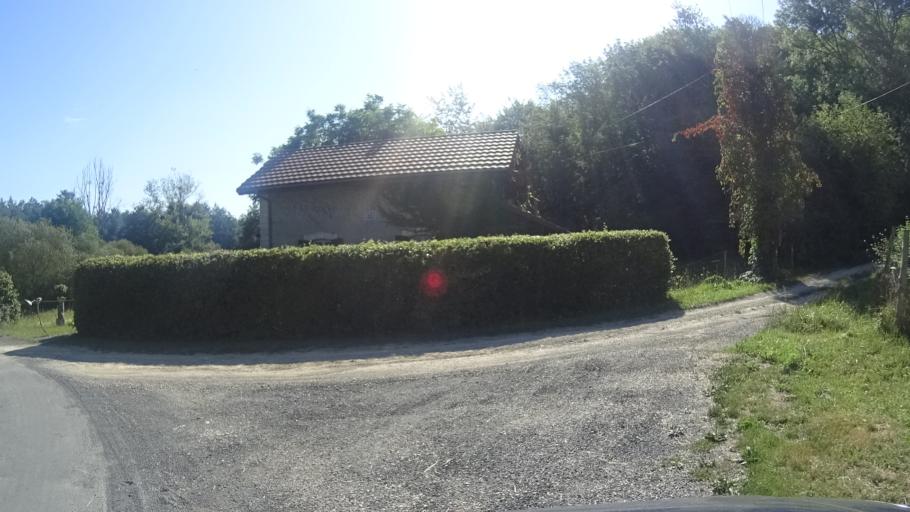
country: FR
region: Aquitaine
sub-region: Departement de la Dordogne
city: Sourzac
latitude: 45.0140
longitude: 0.4385
